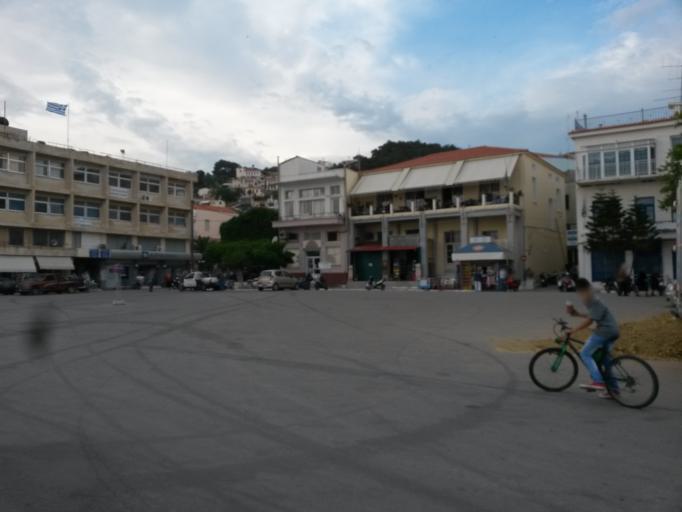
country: GR
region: North Aegean
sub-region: Nomos Lesvou
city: Plomarion
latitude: 38.9747
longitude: 26.3687
